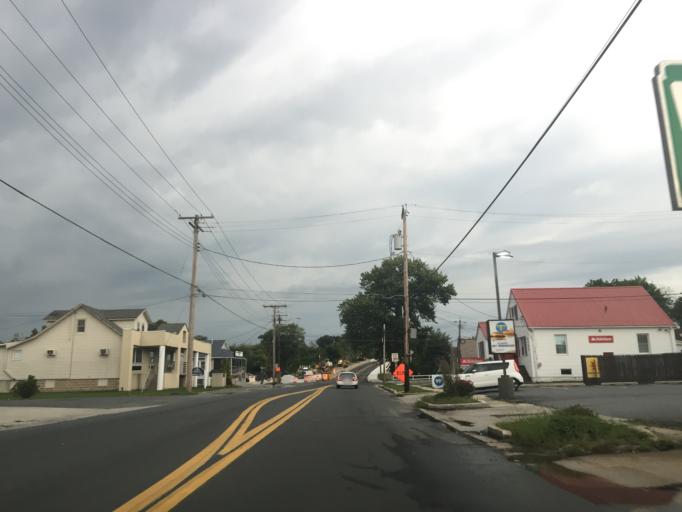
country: US
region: Maryland
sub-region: Baltimore County
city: Parkville
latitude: 39.3906
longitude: -76.5436
